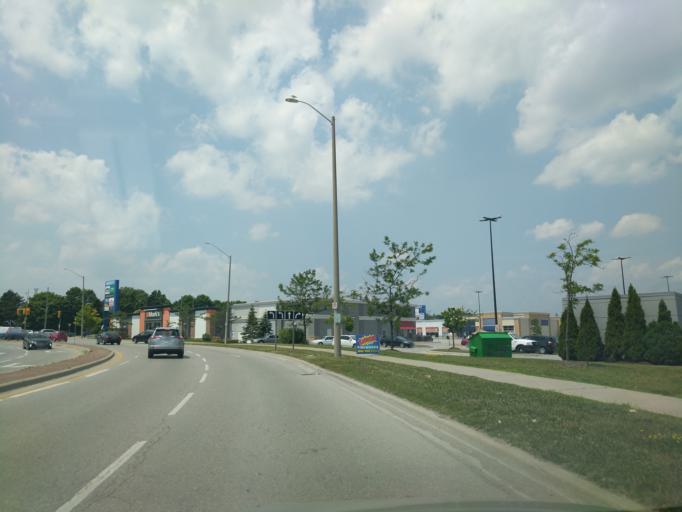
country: CA
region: Ontario
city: Ajax
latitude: 43.8438
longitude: -79.0705
